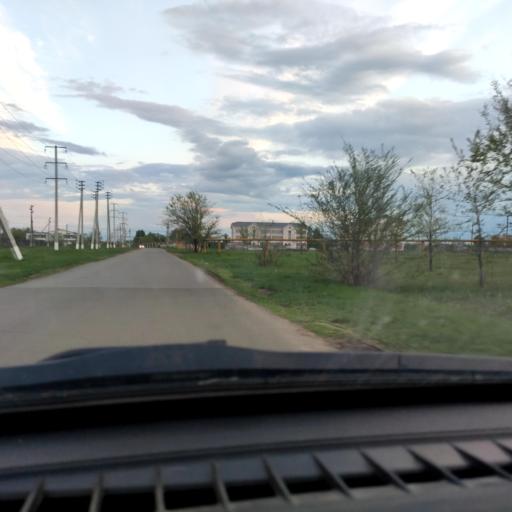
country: RU
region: Samara
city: Podstepki
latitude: 53.5222
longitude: 49.1136
